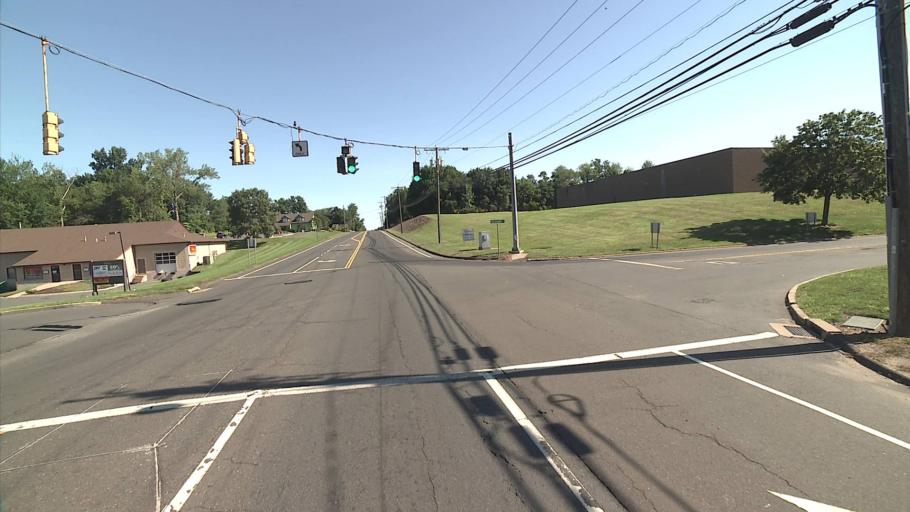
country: US
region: Connecticut
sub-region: New Haven County
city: Cheshire Village
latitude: 41.5485
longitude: -72.8914
